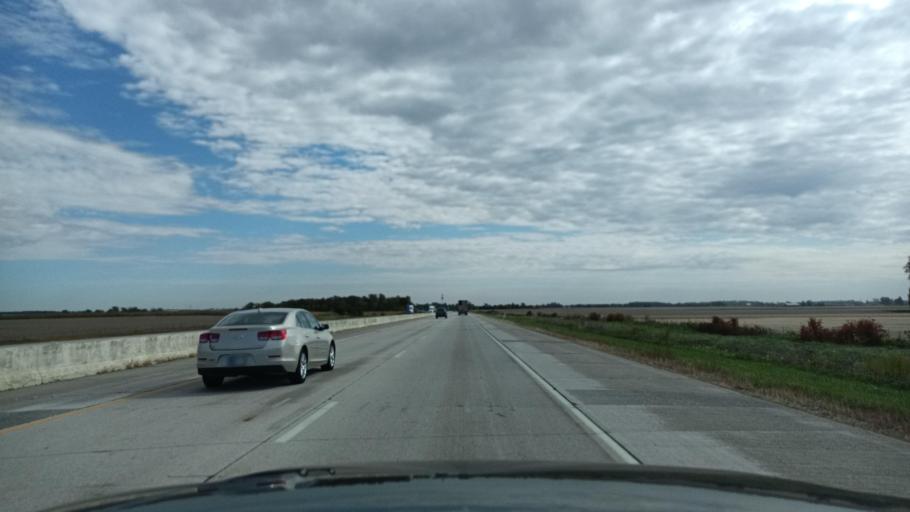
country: US
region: Indiana
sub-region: Wells County
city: Ossian
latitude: 40.9526
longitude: -85.2051
